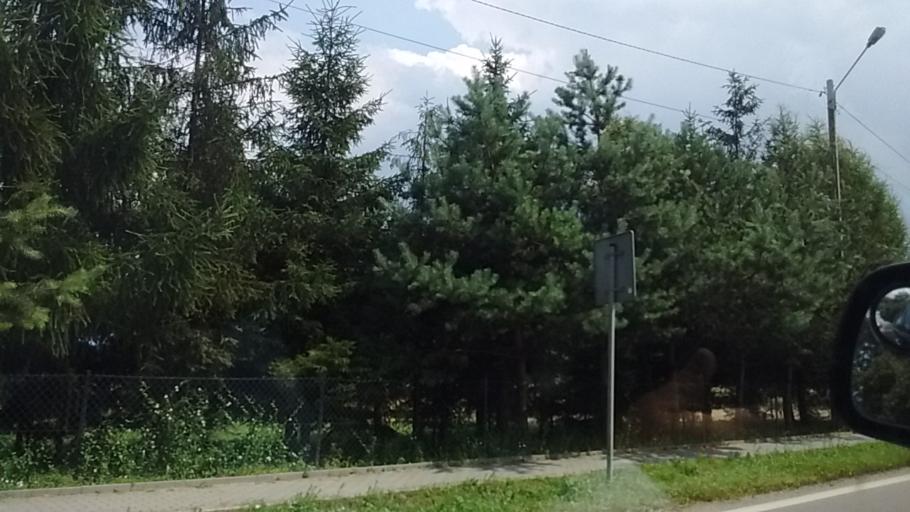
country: PL
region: Subcarpathian Voivodeship
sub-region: Powiat lancucki
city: Lancut
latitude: 50.1119
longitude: 22.2330
